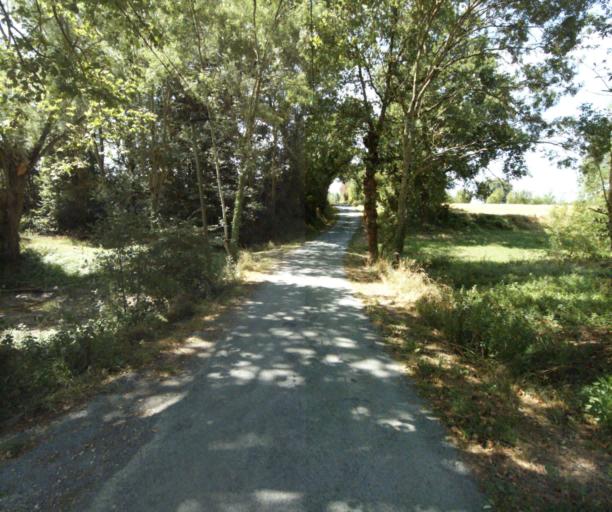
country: FR
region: Midi-Pyrenees
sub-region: Departement du Tarn
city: Puylaurens
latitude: 43.5338
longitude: 2.0062
